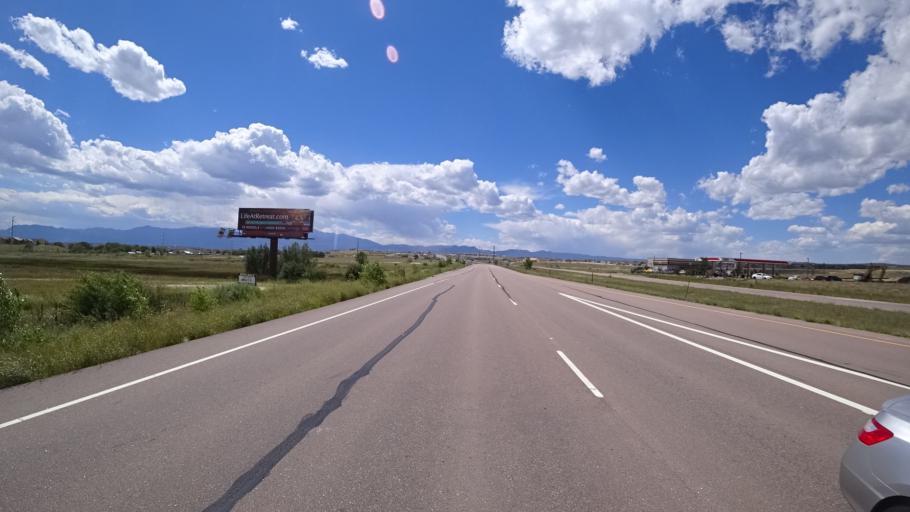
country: US
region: Colorado
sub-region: El Paso County
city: Black Forest
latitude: 38.9408
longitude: -104.6799
